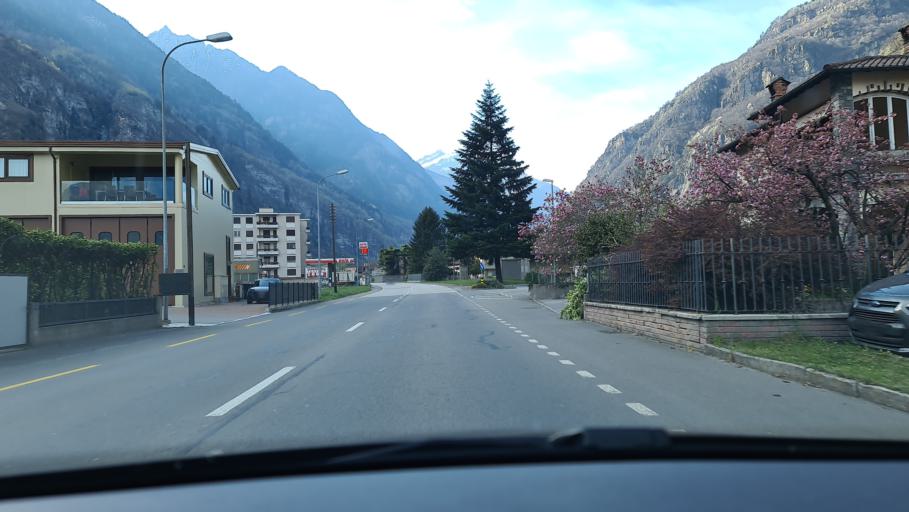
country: CH
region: Ticino
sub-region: Leventina District
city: Bodio
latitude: 46.3754
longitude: 8.9188
